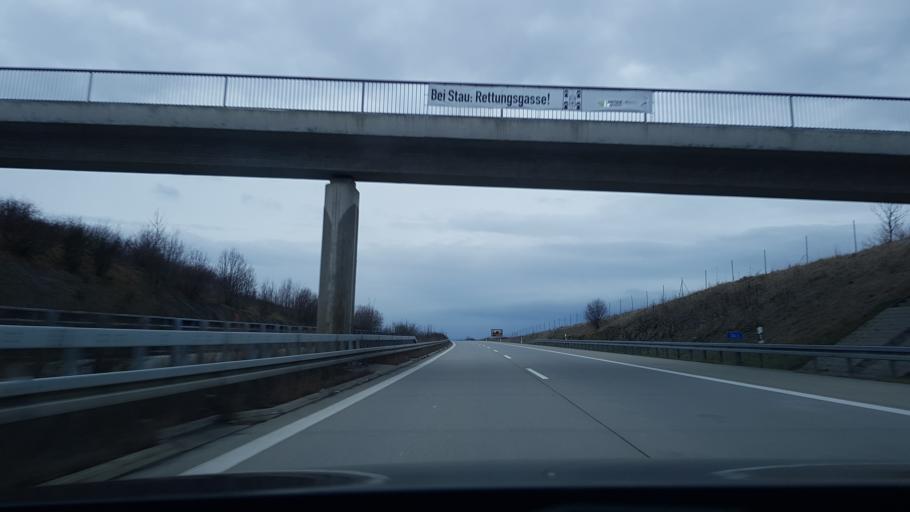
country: DE
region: Saxony
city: Liebstadt
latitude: 50.8510
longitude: 13.8797
